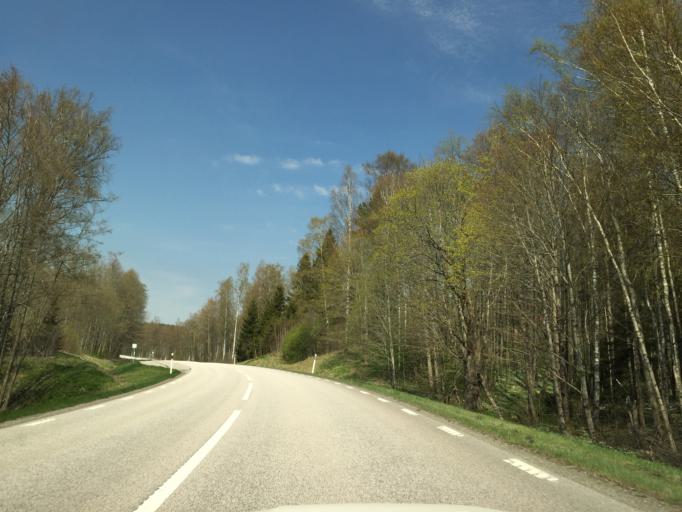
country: SE
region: Vaestra Goetaland
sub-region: Bengtsfors Kommun
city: Dals Langed
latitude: 58.8773
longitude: 12.2147
